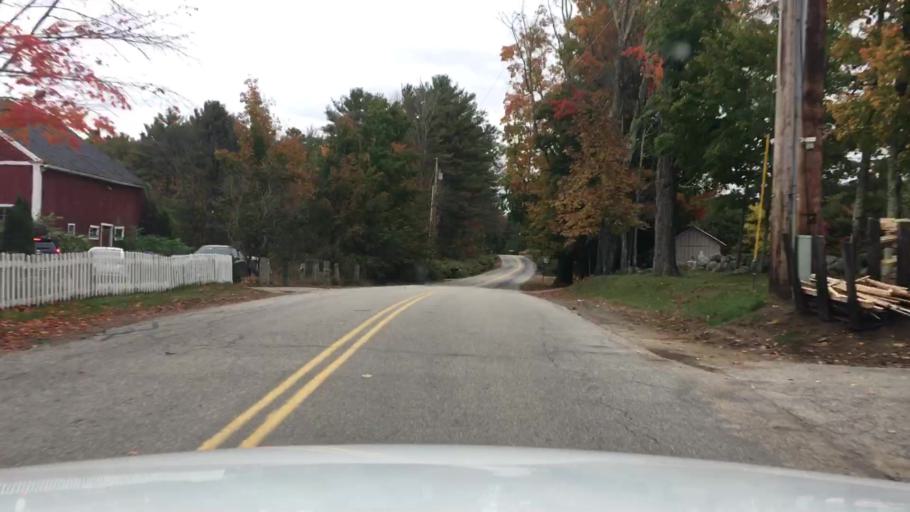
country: US
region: New Hampshire
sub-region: Strafford County
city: Somersworth
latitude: 43.2727
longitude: -70.9118
